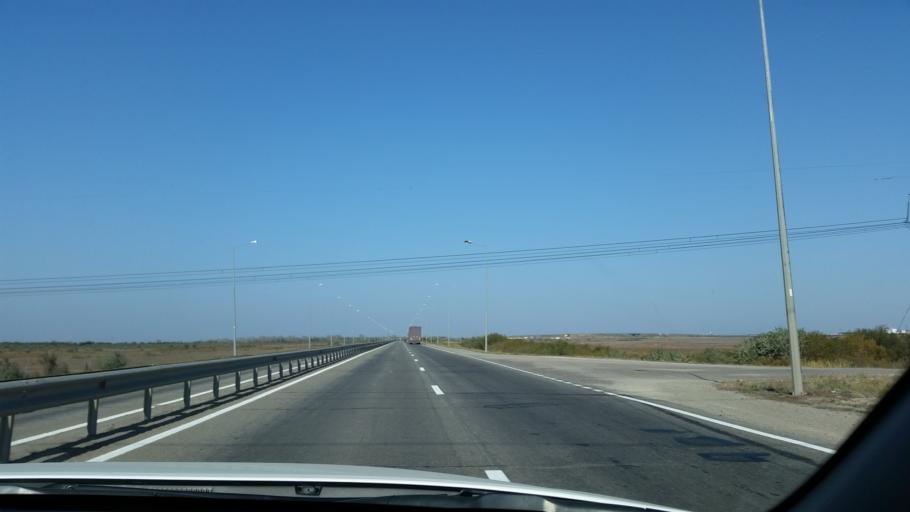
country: KZ
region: Astana Qalasy
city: Astana
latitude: 51.2373
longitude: 71.3317
